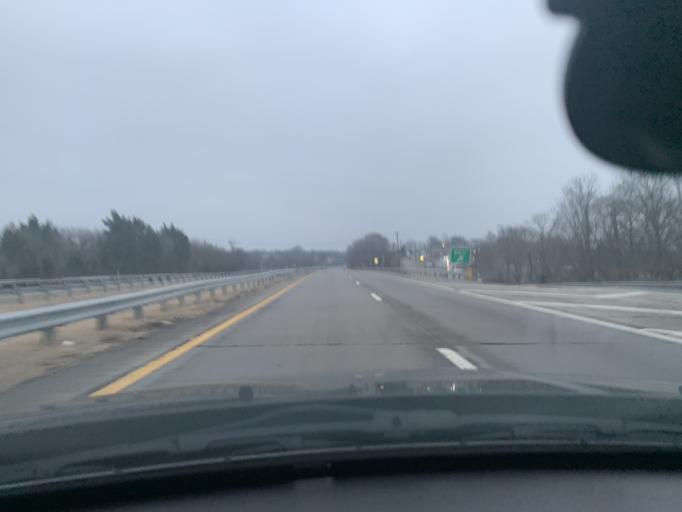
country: US
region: Tennessee
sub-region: Davidson County
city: Nashville
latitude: 36.1952
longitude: -86.7527
